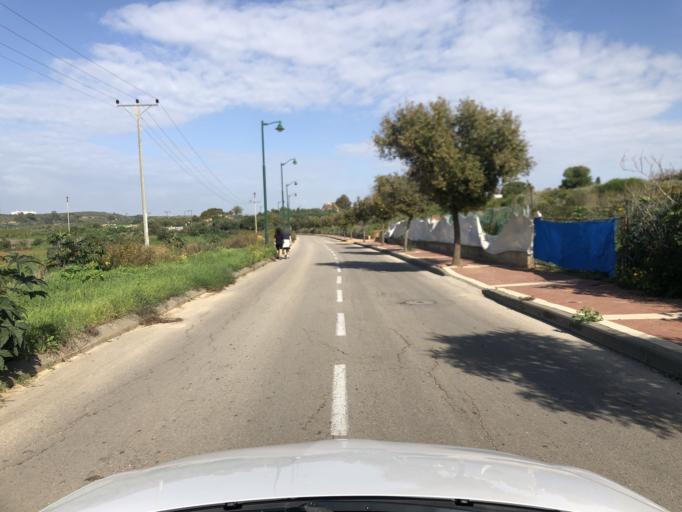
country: IL
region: Central District
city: Ness Ziona
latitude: 31.9120
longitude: 34.7830
